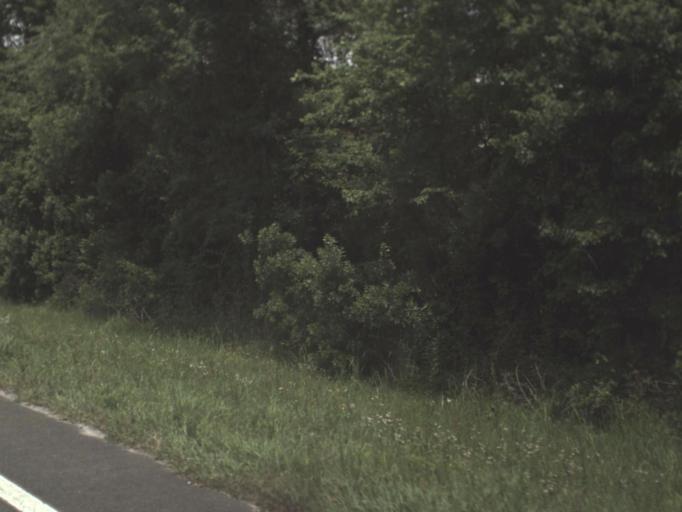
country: US
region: Florida
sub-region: Columbia County
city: Five Points
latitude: 30.2980
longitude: -82.6307
